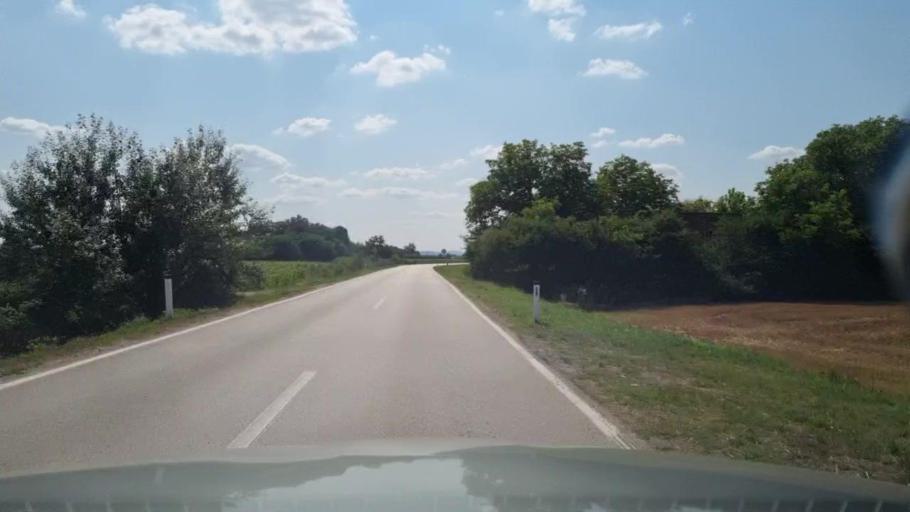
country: BA
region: Federation of Bosnia and Herzegovina
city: Donja Dubica
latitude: 45.0644
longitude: 18.4169
